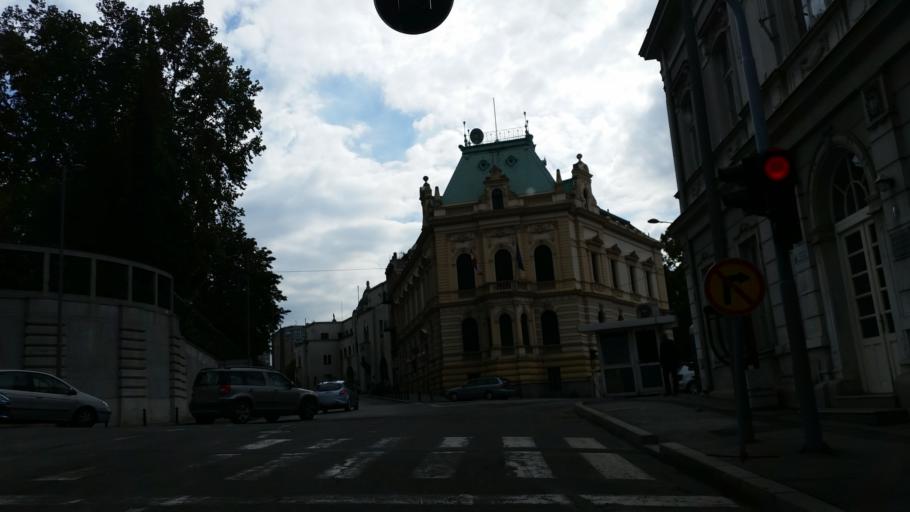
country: RS
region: Central Serbia
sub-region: Belgrade
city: Stari Grad
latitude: 44.8187
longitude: 20.4511
